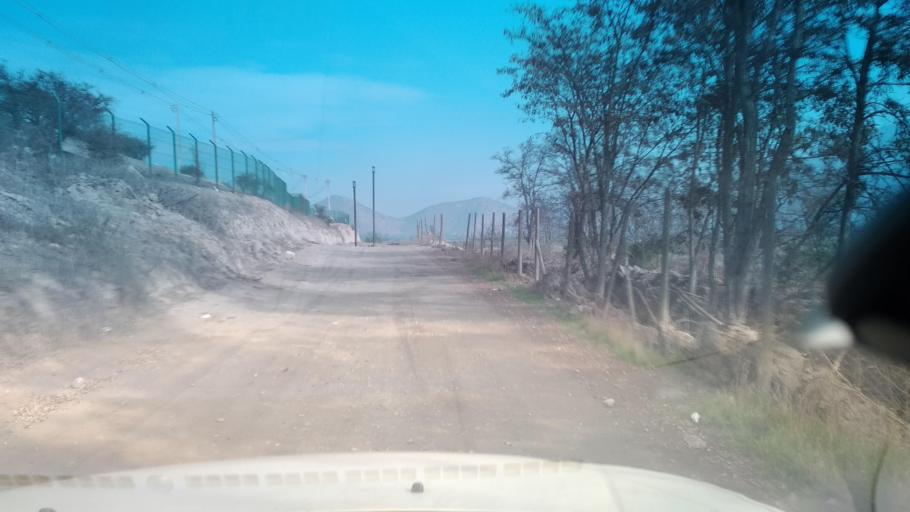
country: CL
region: Santiago Metropolitan
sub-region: Provincia de Santiago
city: Lo Prado
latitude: -33.4645
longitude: -70.7867
